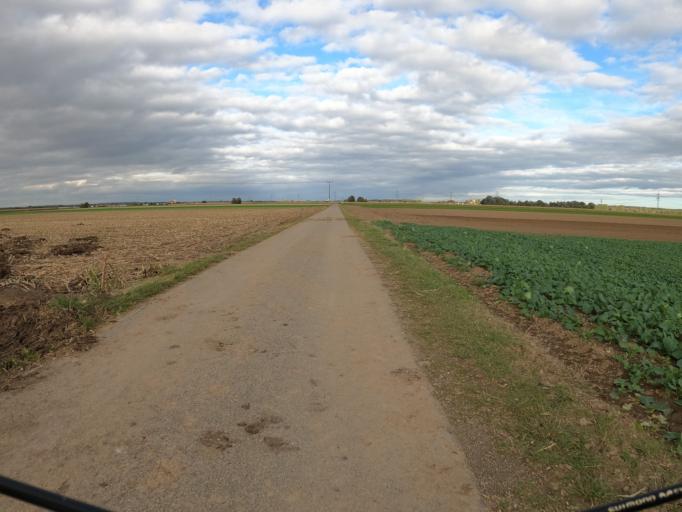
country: DE
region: Bavaria
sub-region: Swabia
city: Holzheim
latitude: 48.4046
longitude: 10.1116
